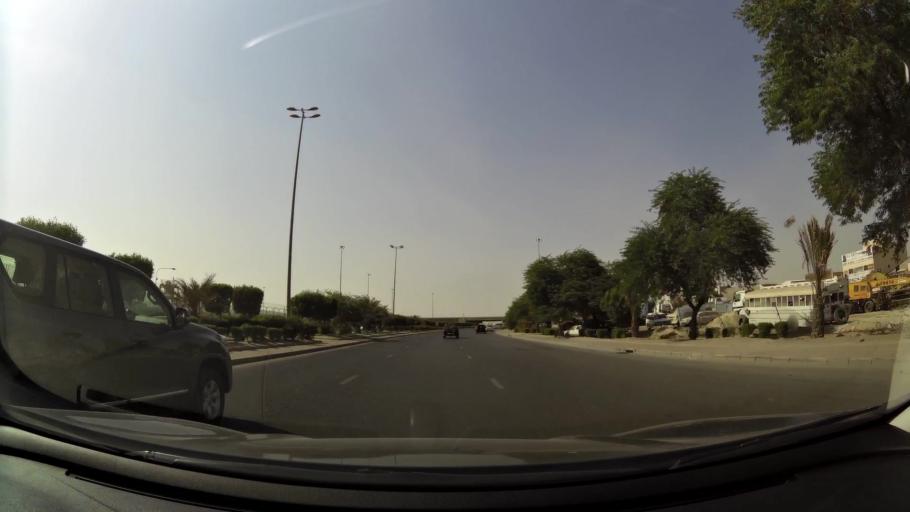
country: KW
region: Al Ahmadi
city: Al Fahahil
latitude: 29.0713
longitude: 48.1149
